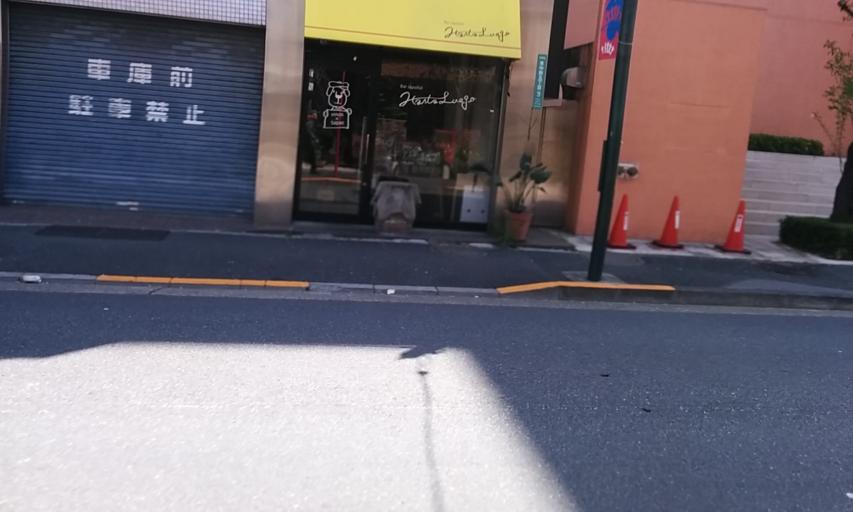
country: JP
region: Tokyo
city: Tokyo
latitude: 35.7085
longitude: 139.6871
